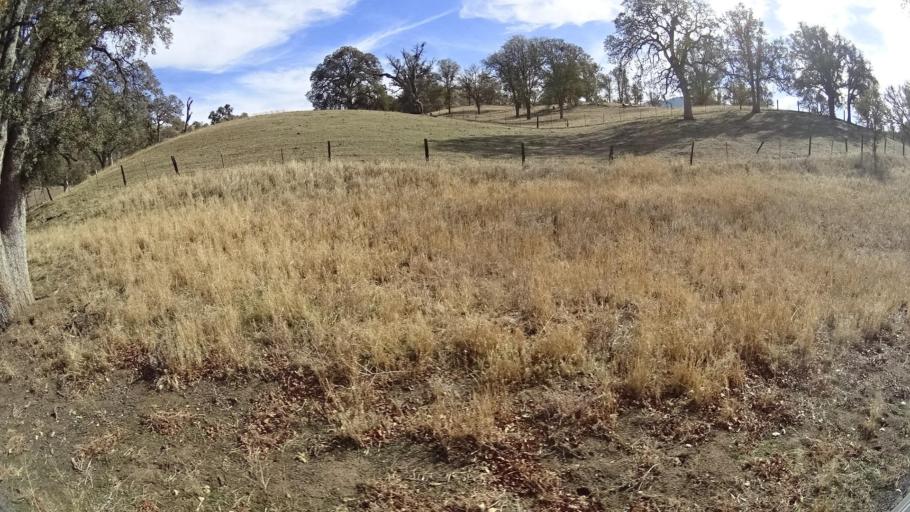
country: US
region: California
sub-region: Kern County
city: Alta Sierra
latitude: 35.6817
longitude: -118.7324
